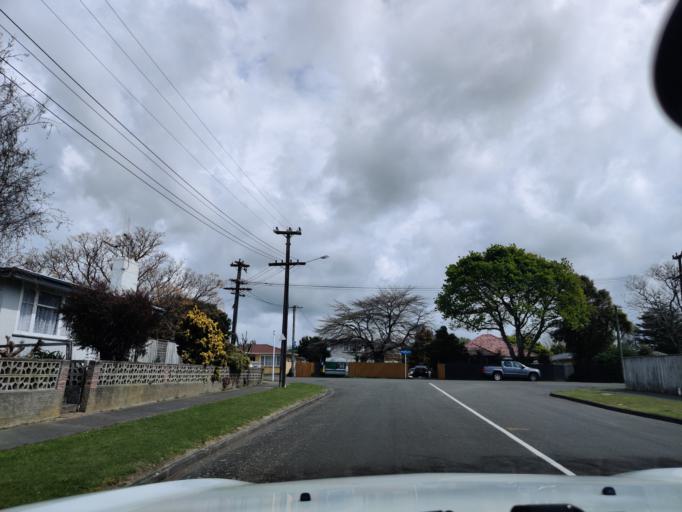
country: NZ
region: Manawatu-Wanganui
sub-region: Palmerston North City
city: Palmerston North
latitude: -40.3811
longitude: 175.5867
